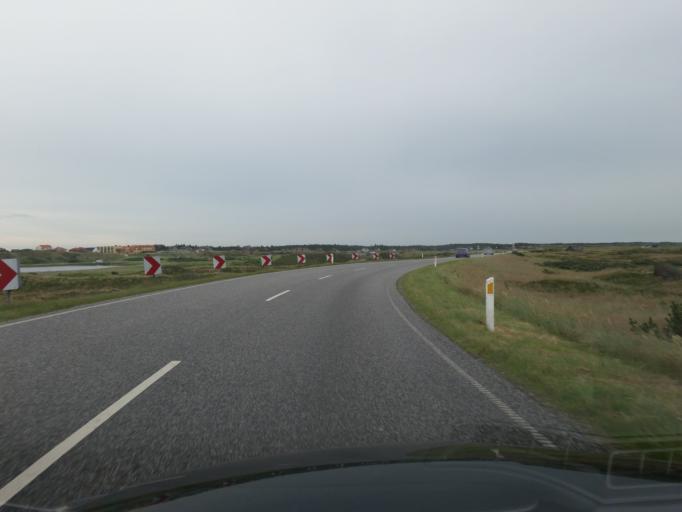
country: DK
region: Central Jutland
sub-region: Ringkobing-Skjern Kommune
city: Hvide Sande
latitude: 55.8223
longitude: 8.1803
